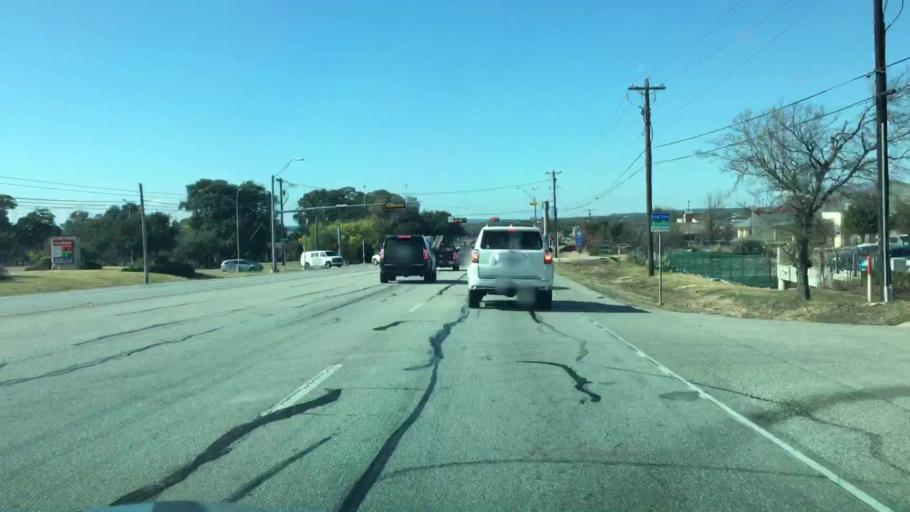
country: US
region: Texas
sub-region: Hays County
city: Dripping Springs
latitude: 30.1926
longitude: -98.0829
